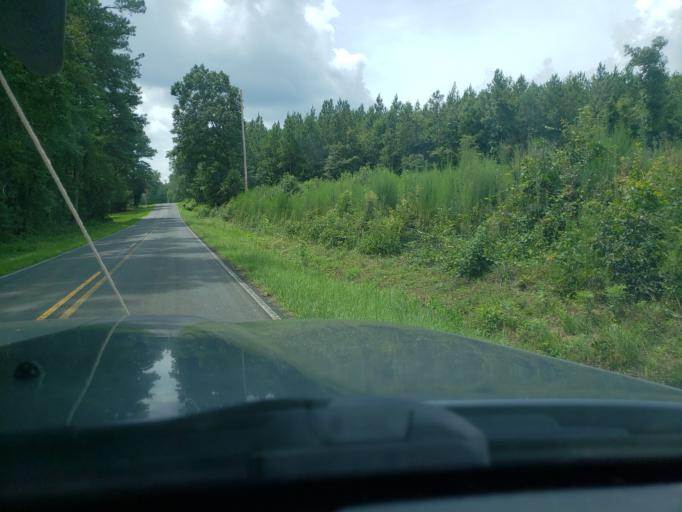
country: US
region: North Carolina
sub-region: Wake County
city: Zebulon
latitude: 35.8942
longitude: -78.3389
